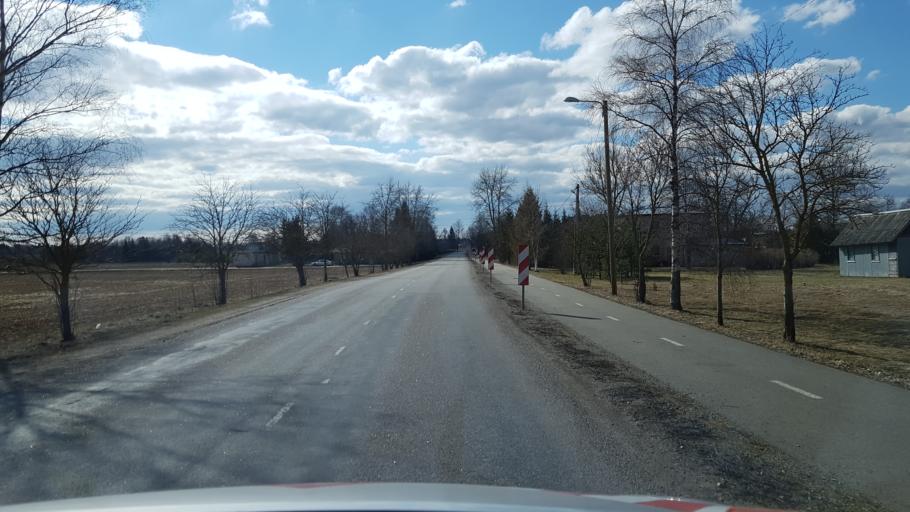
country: EE
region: Laeaene-Virumaa
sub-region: Rakvere linn
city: Rakvere
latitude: 59.3322
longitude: 26.3074
